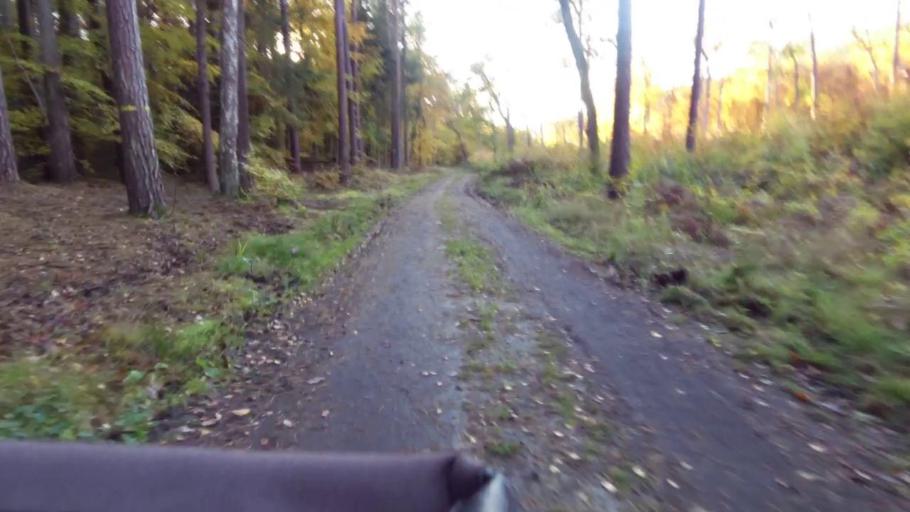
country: PL
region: West Pomeranian Voivodeship
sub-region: Powiat kamienski
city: Miedzyzdroje
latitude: 53.9137
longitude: 14.3930
